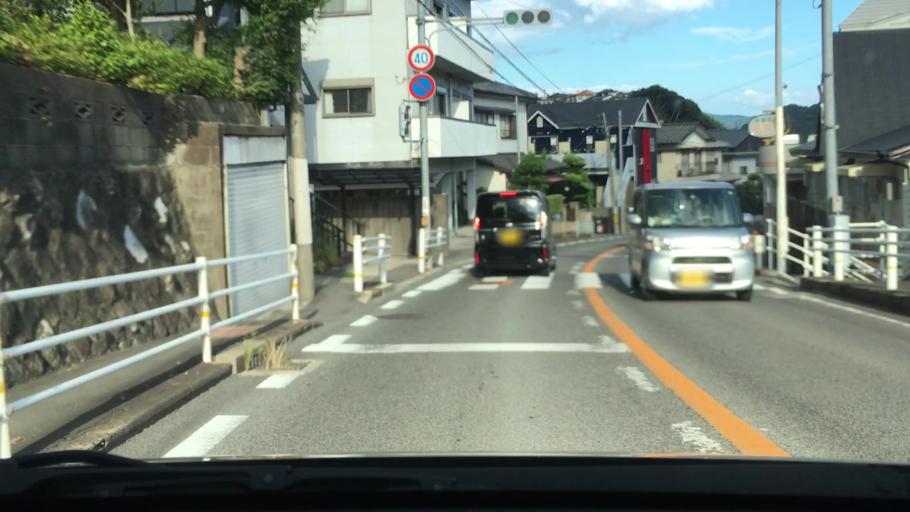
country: JP
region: Nagasaki
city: Togitsu
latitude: 32.8108
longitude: 129.8275
